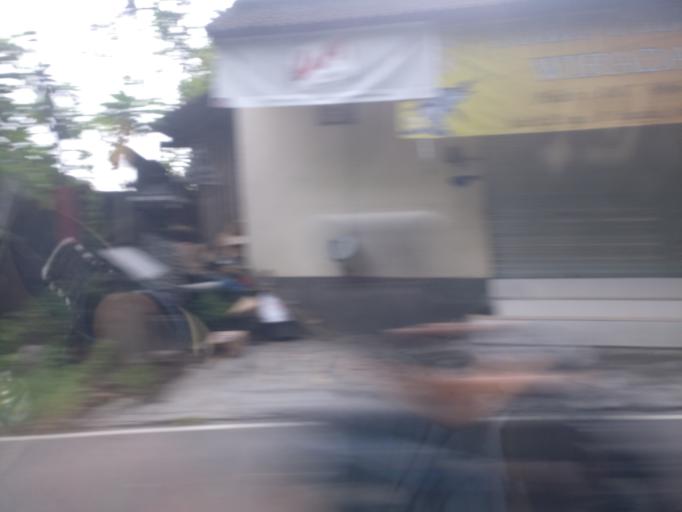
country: ID
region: Bali
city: Padangbai
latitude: -8.5192
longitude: 115.4981
